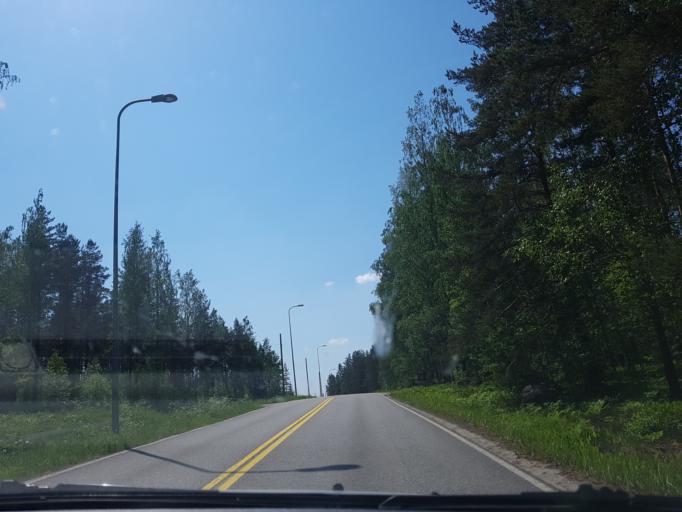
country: FI
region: Uusimaa
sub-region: Helsinki
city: Vihti
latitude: 60.3333
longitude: 24.4292
